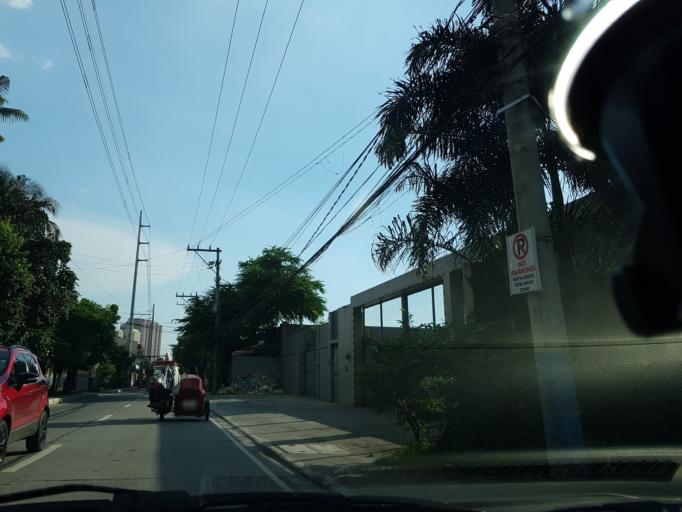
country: PH
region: Metro Manila
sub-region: Marikina
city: Calumpang
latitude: 14.6206
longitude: 121.0827
